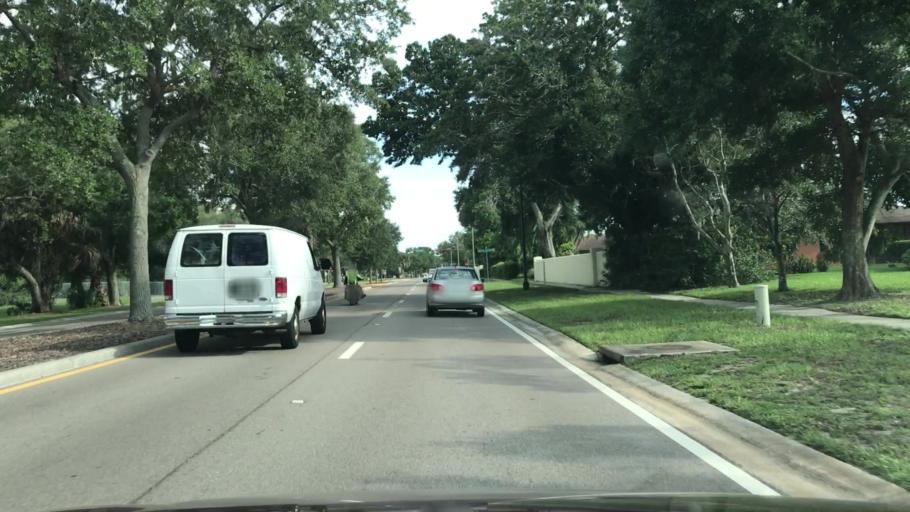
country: US
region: Florida
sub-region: Sarasota County
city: Plantation
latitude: 27.0741
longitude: -82.3890
